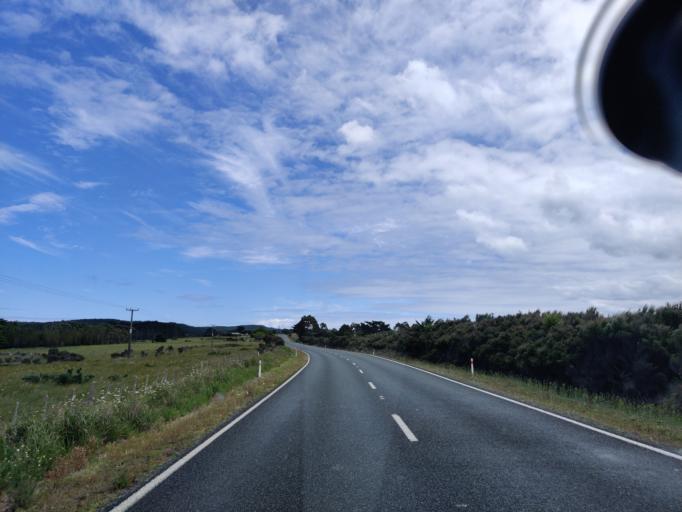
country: NZ
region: Northland
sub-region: Far North District
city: Kaitaia
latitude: -34.6726
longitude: 172.9948
